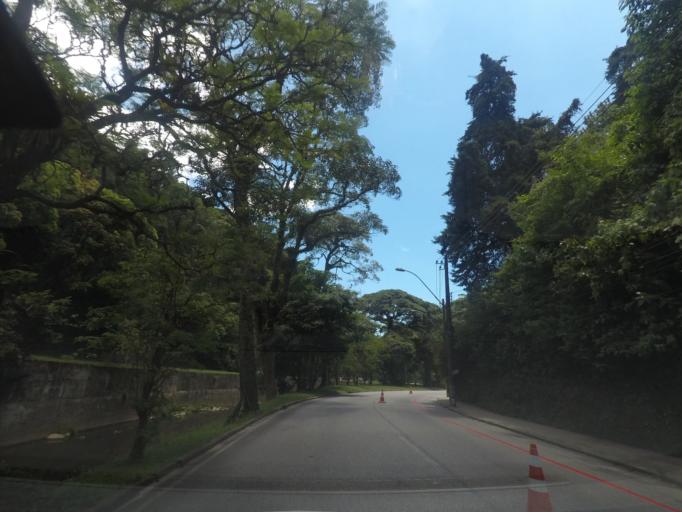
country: BR
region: Rio de Janeiro
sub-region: Petropolis
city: Petropolis
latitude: -22.5009
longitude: -43.1813
